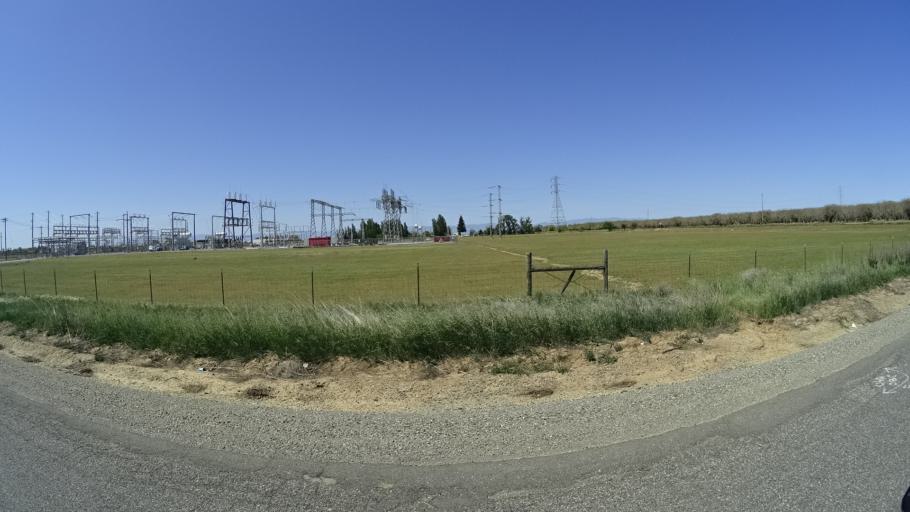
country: US
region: California
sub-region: Glenn County
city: Orland
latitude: 39.7784
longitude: -122.1407
